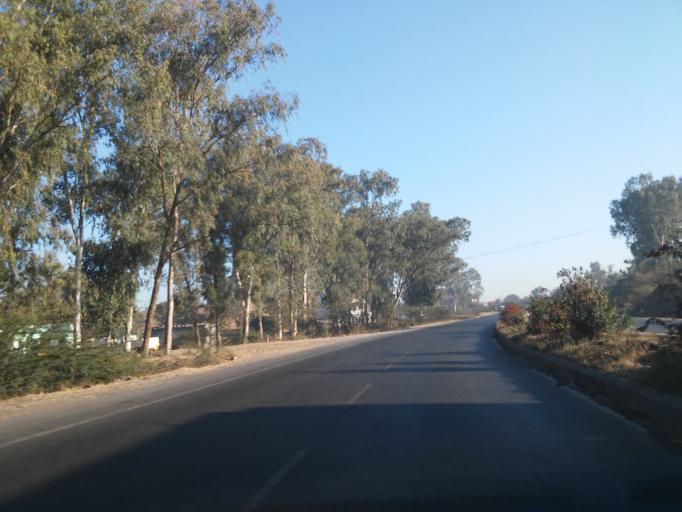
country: IN
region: Rajasthan
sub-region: Dungarpur
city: Dungarpur
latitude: 23.8786
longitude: 73.5314
